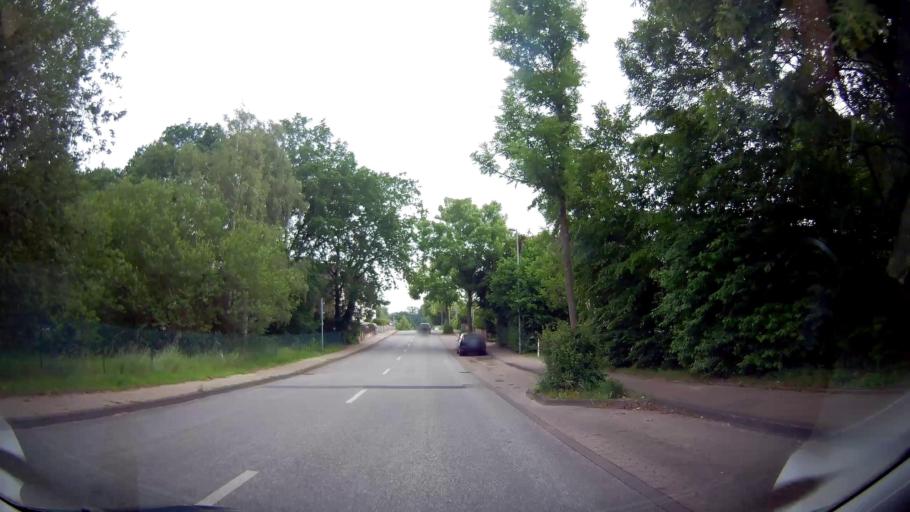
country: DE
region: North Rhine-Westphalia
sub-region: Regierungsbezirk Detmold
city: Herford
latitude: 52.1270
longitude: 8.7031
